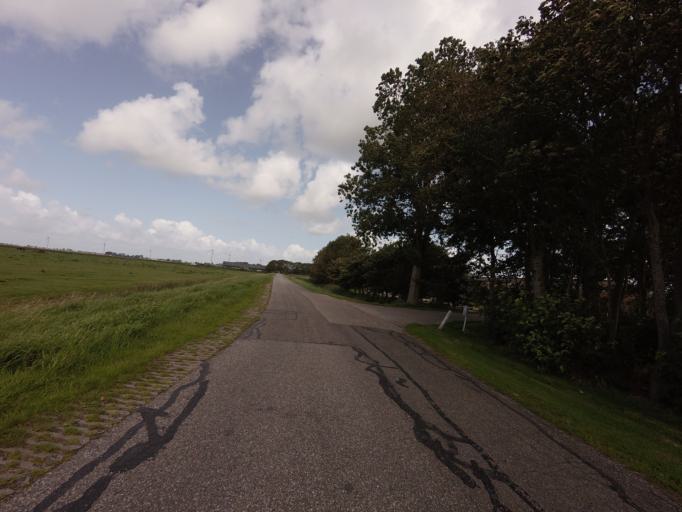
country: NL
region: Friesland
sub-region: Gemeente Franekeradeel
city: Sexbierum
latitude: 53.1699
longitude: 5.4884
